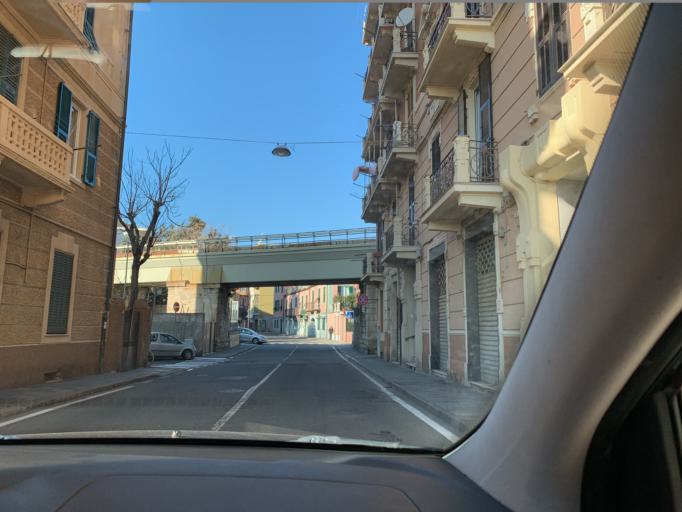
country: IT
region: Liguria
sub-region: Provincia di Savona
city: Savona
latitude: 44.3005
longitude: 8.4744
